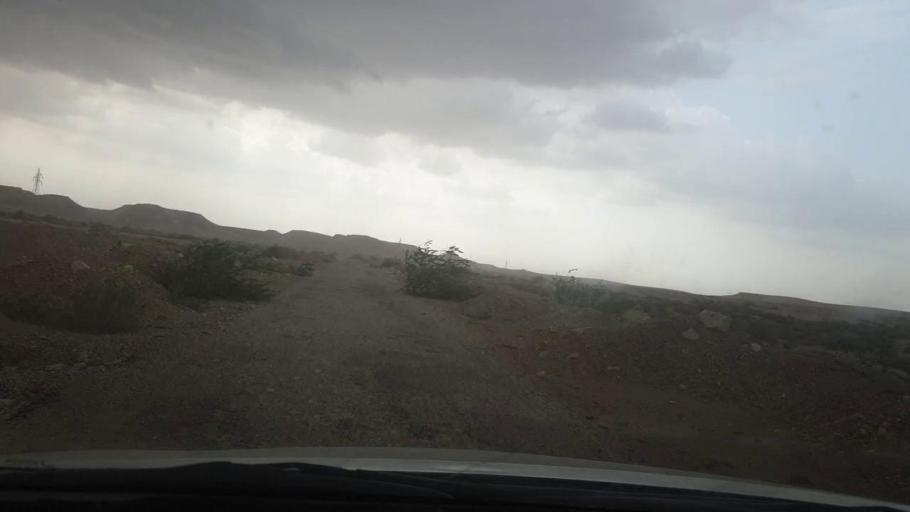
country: PK
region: Sindh
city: Khairpur
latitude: 27.4422
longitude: 68.9668
